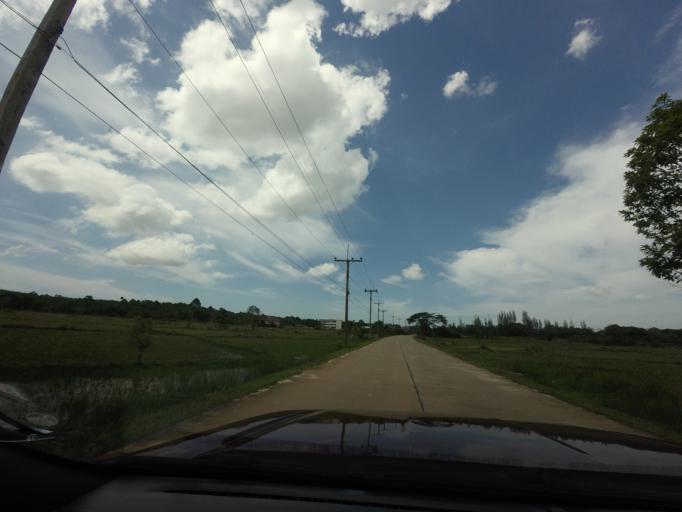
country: TH
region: Narathiwat
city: Bacho
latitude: 6.4864
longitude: 101.6613
